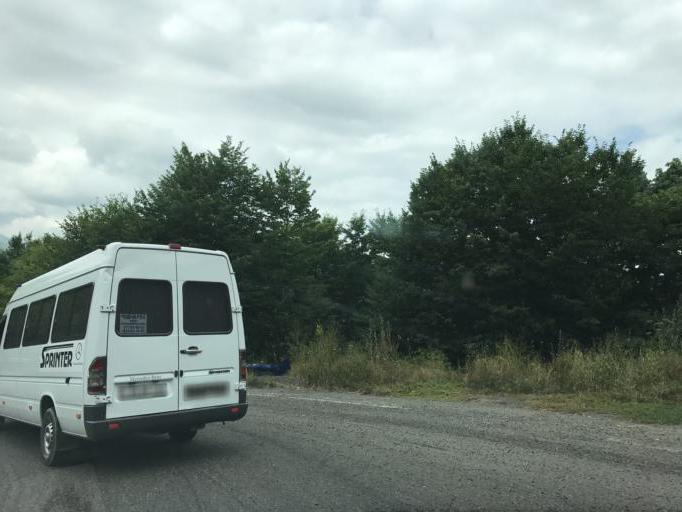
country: AM
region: Tavush
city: Dilijan
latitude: 40.7016
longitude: 44.8544
